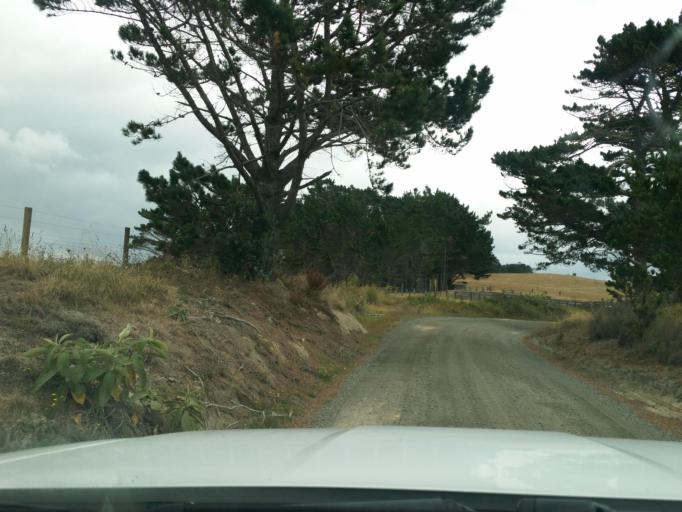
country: NZ
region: Northland
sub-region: Kaipara District
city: Dargaville
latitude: -35.9882
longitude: 173.8195
